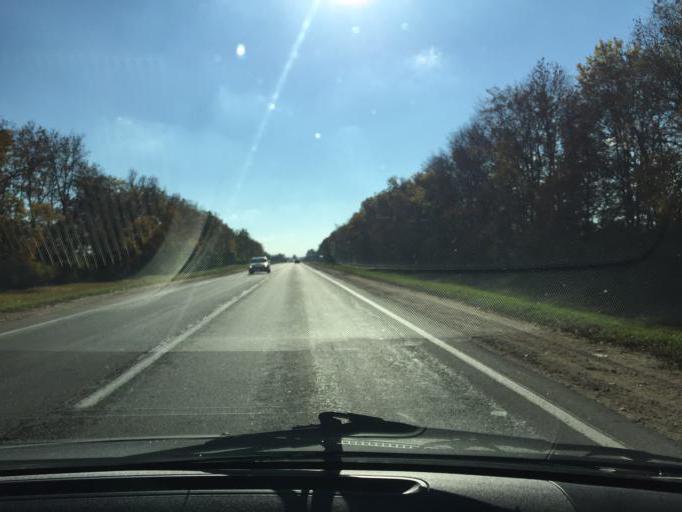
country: BY
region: Minsk
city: Slutsk
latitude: 52.9626
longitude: 27.4982
